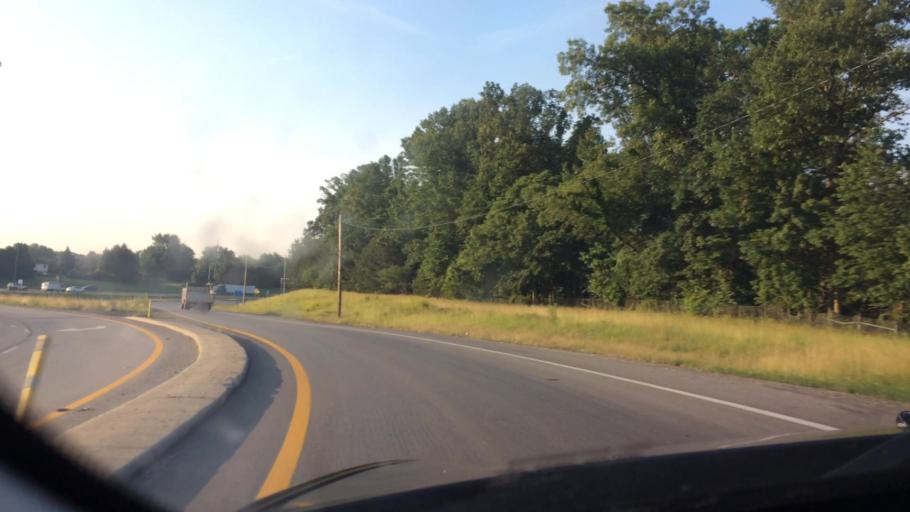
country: US
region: Ohio
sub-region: Lucas County
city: Holland
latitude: 41.6116
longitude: -83.6936
